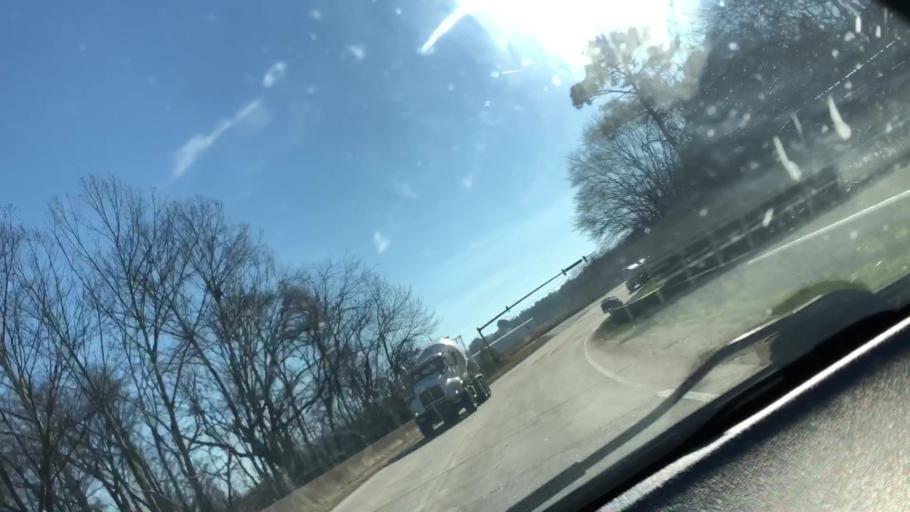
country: US
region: Georgia
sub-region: Bartow County
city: Cartersville
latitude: 34.2214
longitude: -84.8028
